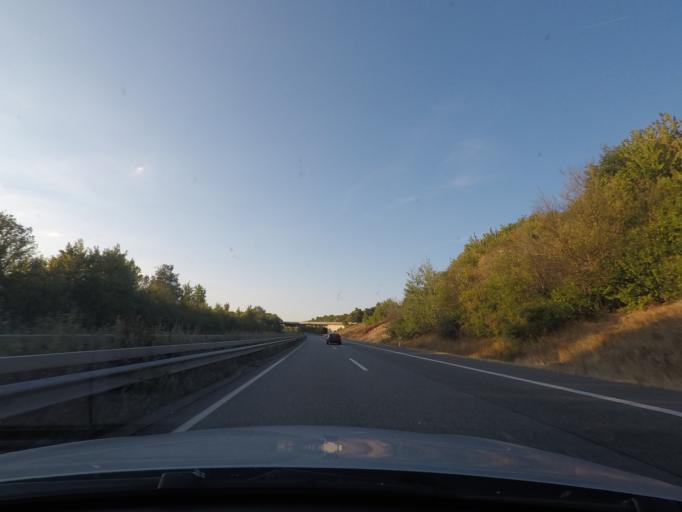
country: DE
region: Rheinland-Pfalz
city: Marnheim
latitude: 49.6377
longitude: 8.0339
